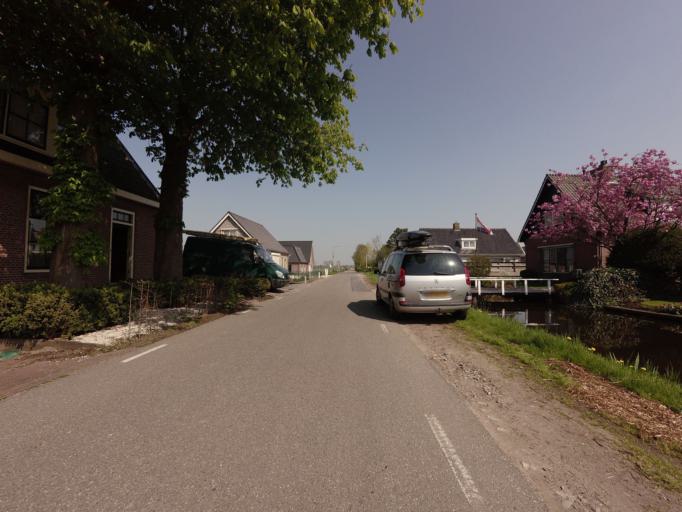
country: NL
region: Utrecht
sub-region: Gemeente De Ronde Venen
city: Mijdrecht
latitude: 52.2269
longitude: 4.9194
